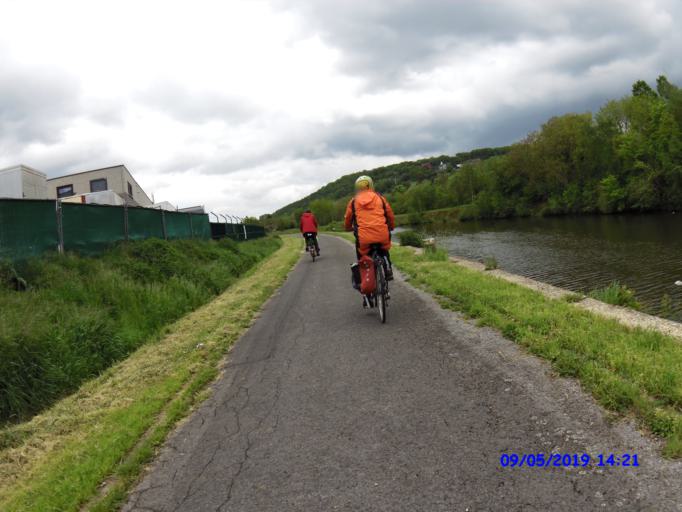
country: BE
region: Wallonia
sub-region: Province du Hainaut
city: Aiseau
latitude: 50.4274
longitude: 4.6024
